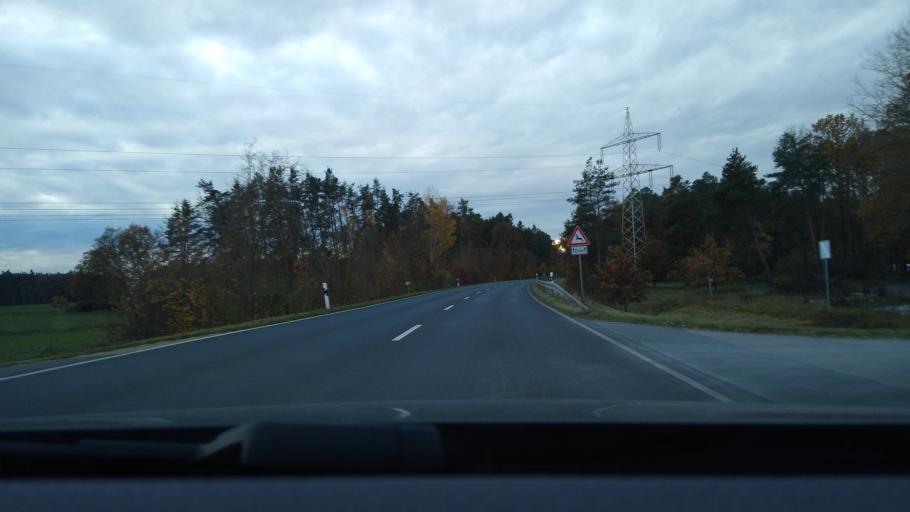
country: DE
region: Bavaria
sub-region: Regierungsbezirk Mittelfranken
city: Rednitzhembach
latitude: 49.3529
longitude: 11.0887
